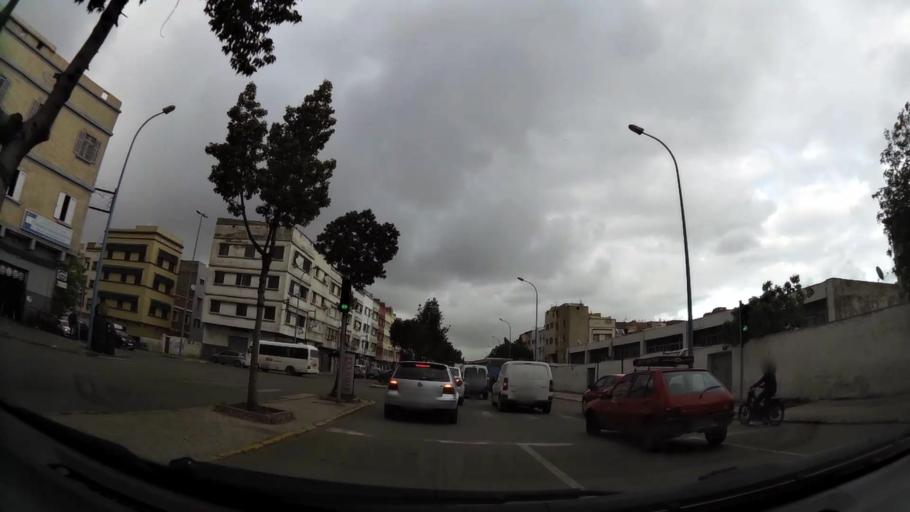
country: MA
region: Grand Casablanca
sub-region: Casablanca
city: Casablanca
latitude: 33.5546
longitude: -7.6001
